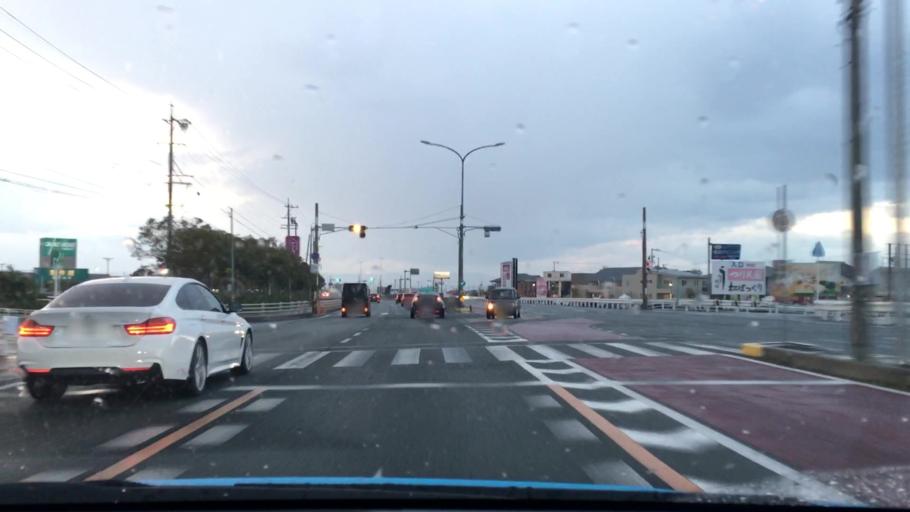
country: JP
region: Mie
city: Ise
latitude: 34.5823
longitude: 136.6168
